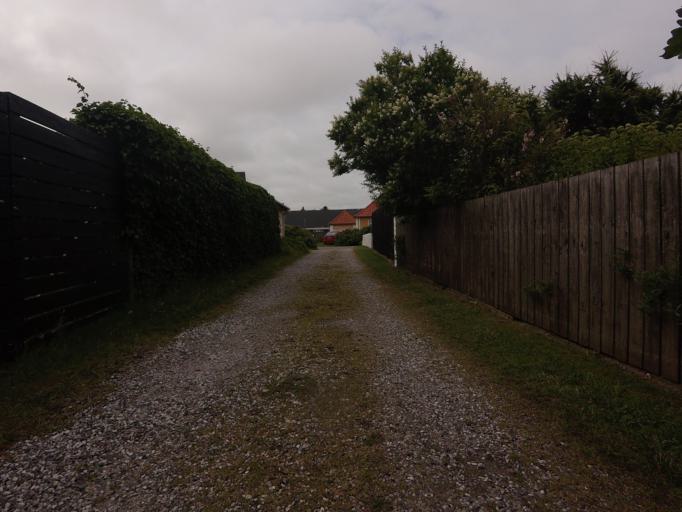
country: DK
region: North Denmark
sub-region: Jammerbugt Kommune
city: Pandrup
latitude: 57.3687
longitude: 9.7095
